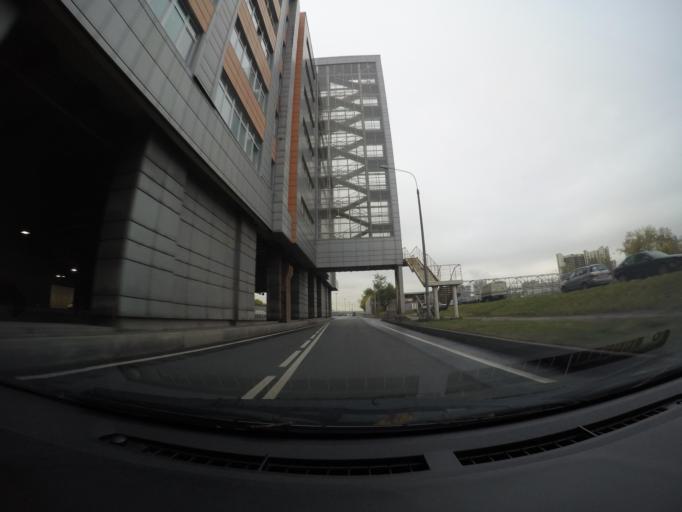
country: RU
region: Moscow
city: Lefortovo
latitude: 55.7748
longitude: 37.7453
